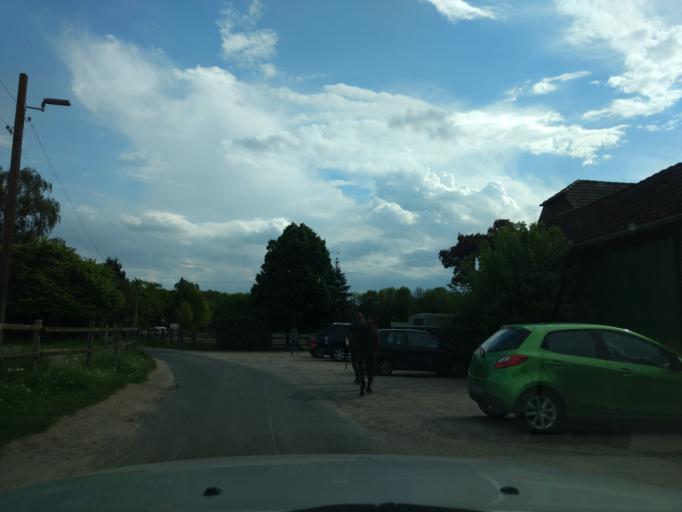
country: DE
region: North Rhine-Westphalia
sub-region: Regierungsbezirk Dusseldorf
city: Willich
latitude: 51.2426
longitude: 6.5015
